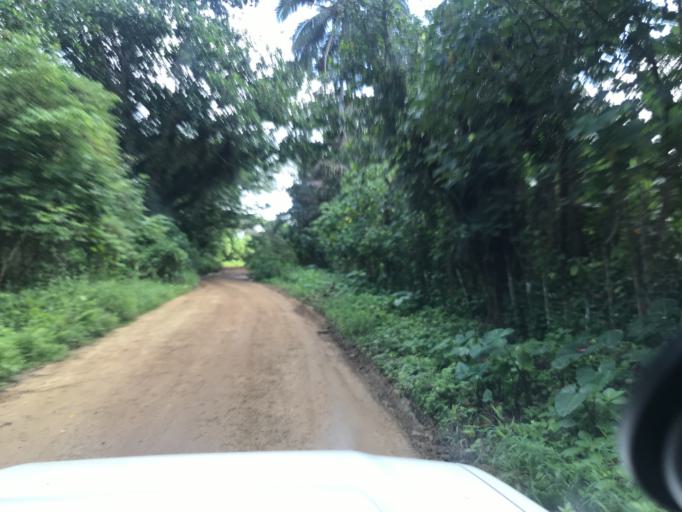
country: VU
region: Sanma
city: Luganville
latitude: -15.4875
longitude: 167.0897
